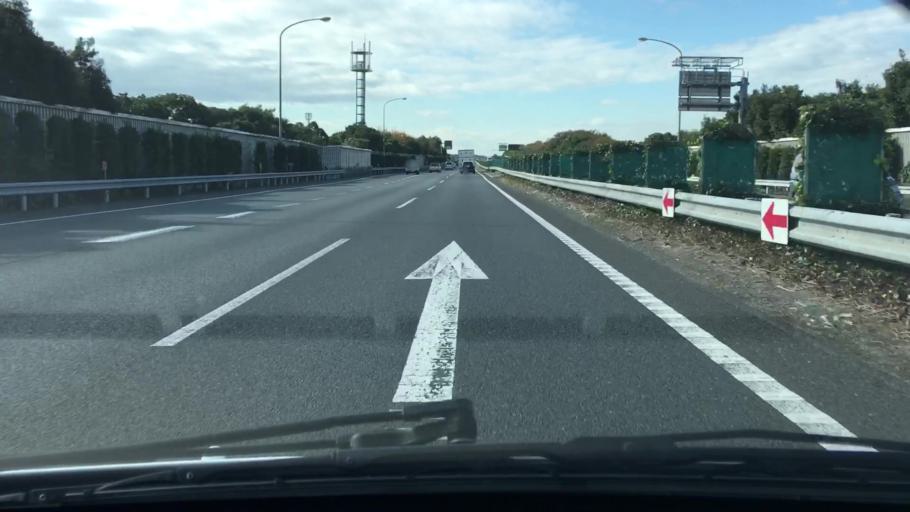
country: JP
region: Chiba
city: Ichihara
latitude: 35.4945
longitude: 140.0912
